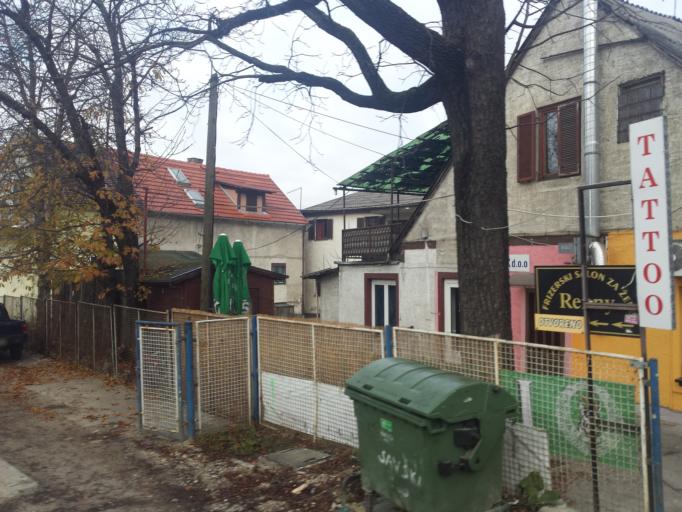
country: HR
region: Grad Zagreb
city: Novi Zagreb
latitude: 45.7896
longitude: 15.9555
